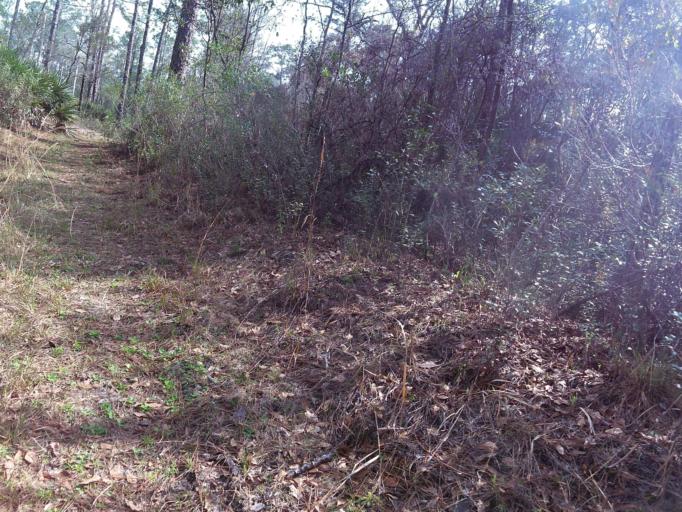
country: US
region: Florida
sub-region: Clay County
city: Middleburg
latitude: 30.1203
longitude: -81.9069
